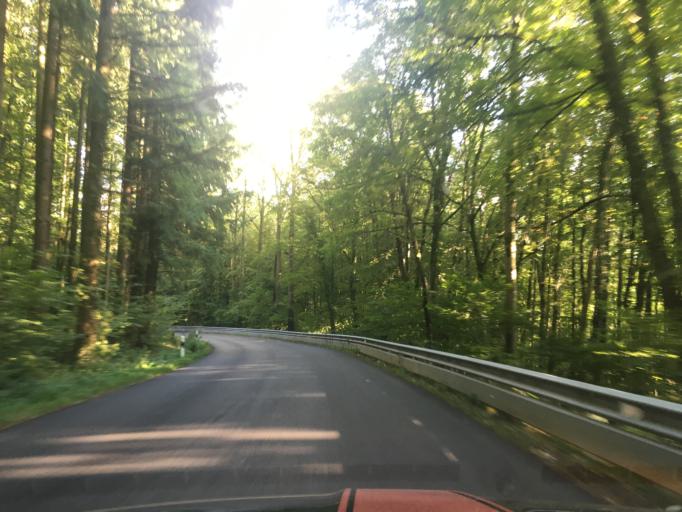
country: FR
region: Lorraine
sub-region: Departement de Meurthe-et-Moselle
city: Hussigny-Godbrange
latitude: 49.5029
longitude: 5.8663
